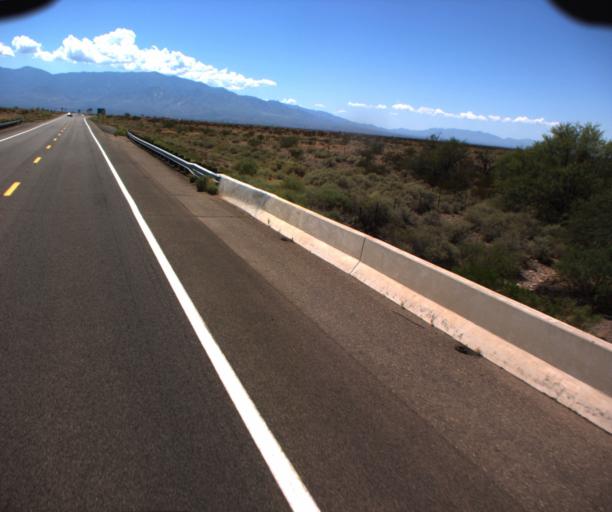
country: US
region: Arizona
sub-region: Graham County
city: Safford
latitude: 32.7939
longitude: -109.5449
